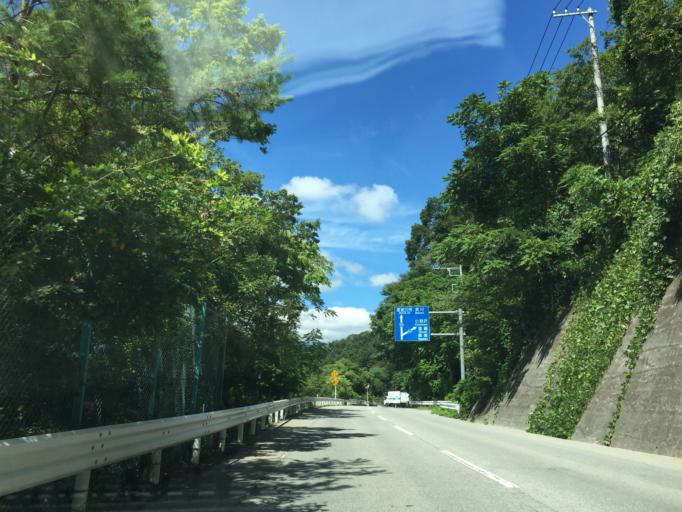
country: JP
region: Yamanashi
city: Nirasaki
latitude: 35.7878
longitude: 138.3911
